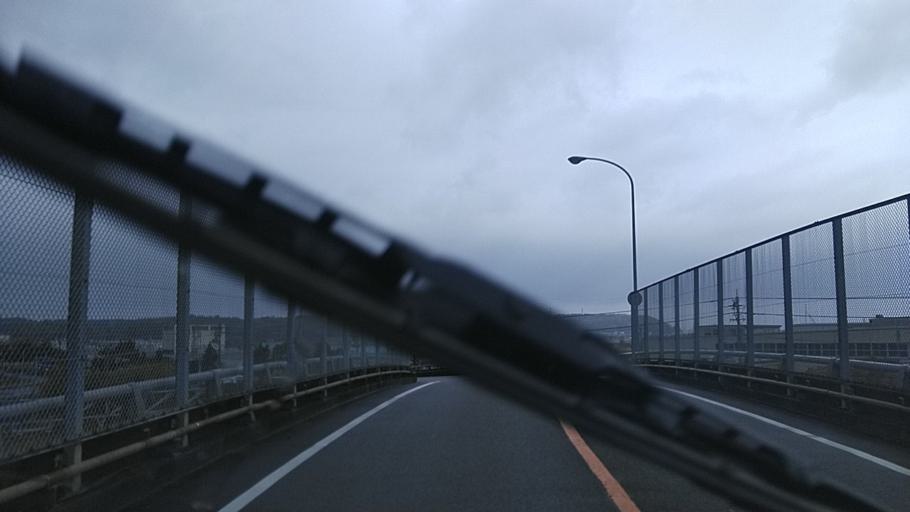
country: JP
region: Ishikawa
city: Komatsu
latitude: 36.3263
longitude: 136.3785
